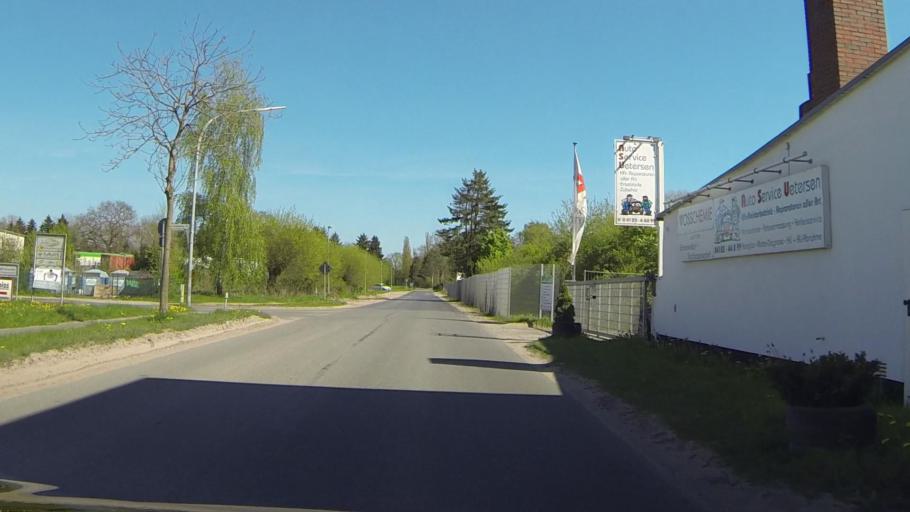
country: DE
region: Schleswig-Holstein
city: Tornesch
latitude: 53.6777
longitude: 9.6960
